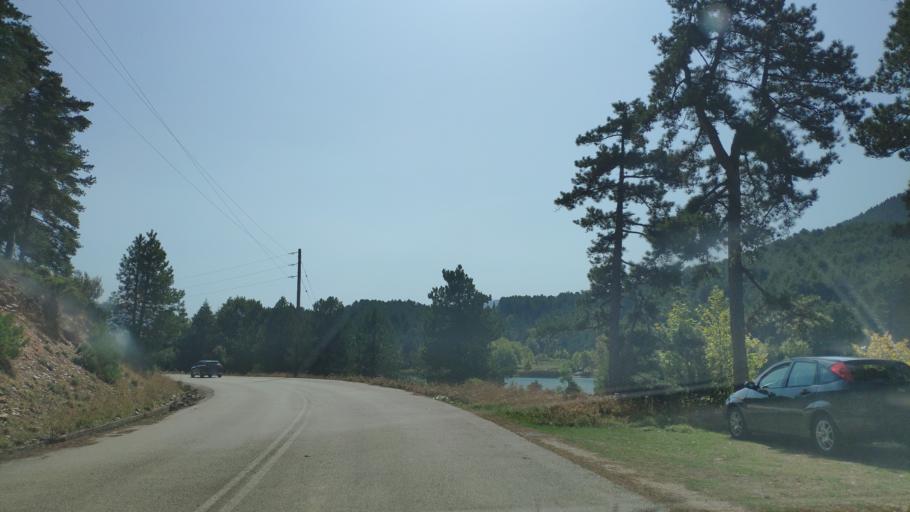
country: GR
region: West Greece
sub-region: Nomos Achaias
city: Kalavryta
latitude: 37.9278
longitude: 22.2913
